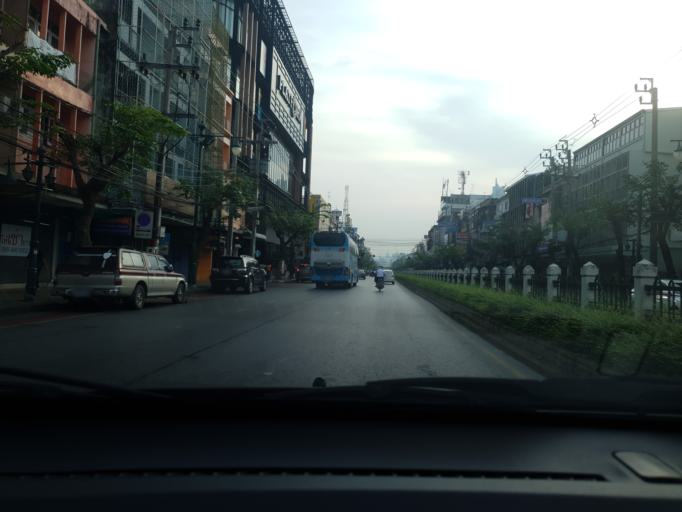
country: TH
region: Bangkok
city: Thon Buri
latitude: 13.7266
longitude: 100.4942
